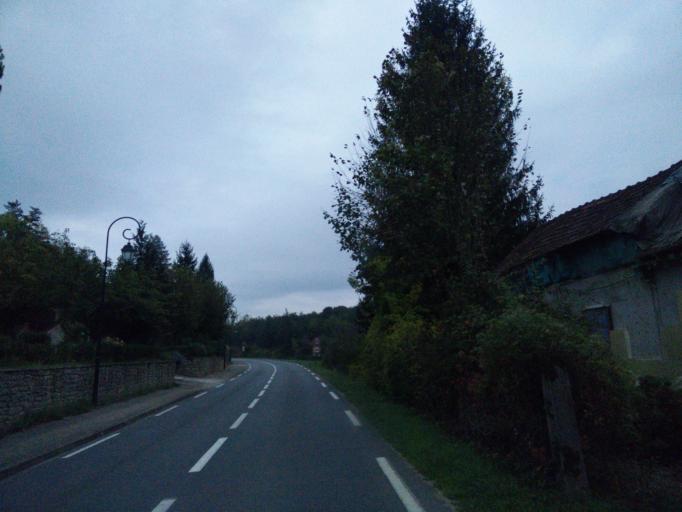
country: FR
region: Aquitaine
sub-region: Departement de la Dordogne
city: Carsac-Aillac
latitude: 44.8125
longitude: 1.2943
